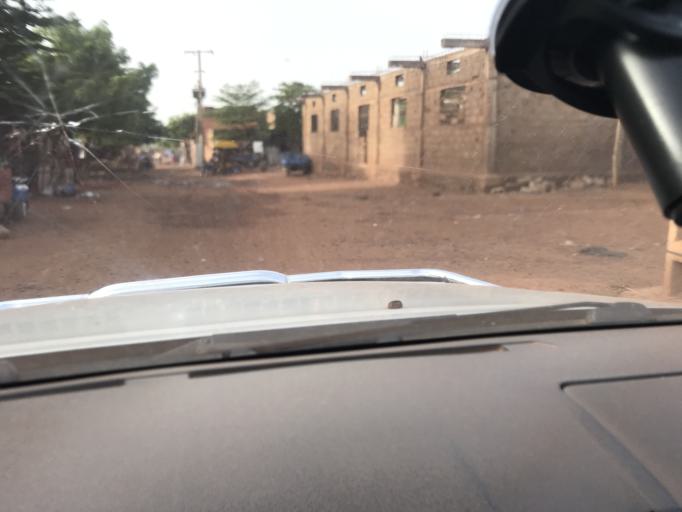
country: ML
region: Bamako
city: Bamako
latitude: 12.5935
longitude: -8.0078
